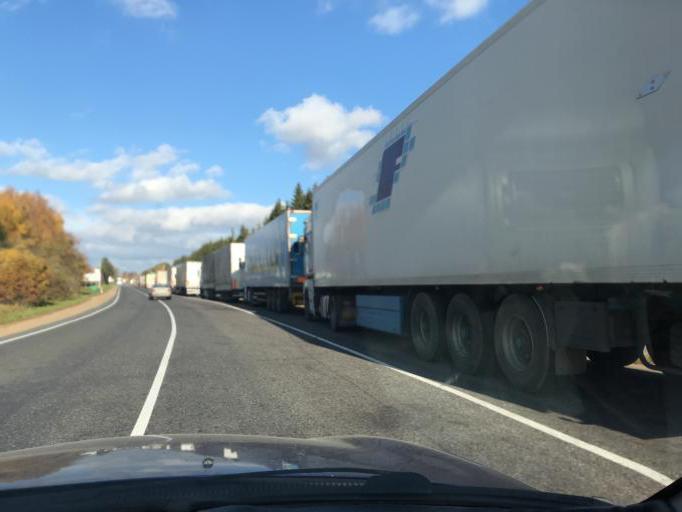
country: LT
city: Salcininkai
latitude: 54.2299
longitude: 25.3589
